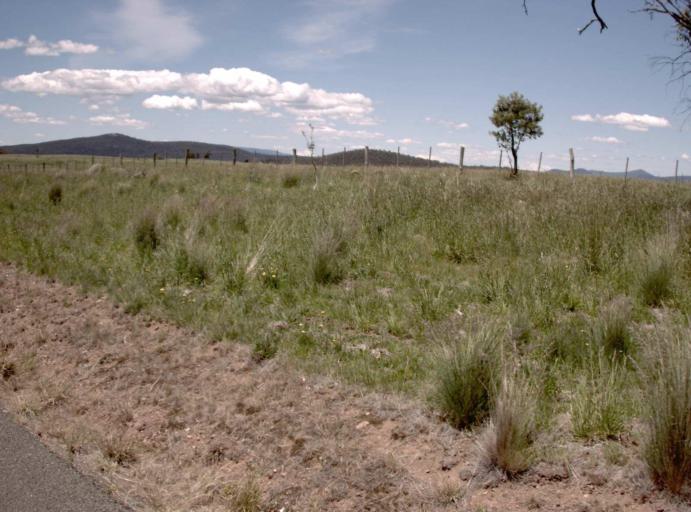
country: AU
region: New South Wales
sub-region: Snowy River
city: Jindabyne
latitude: -37.0892
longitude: 148.2692
